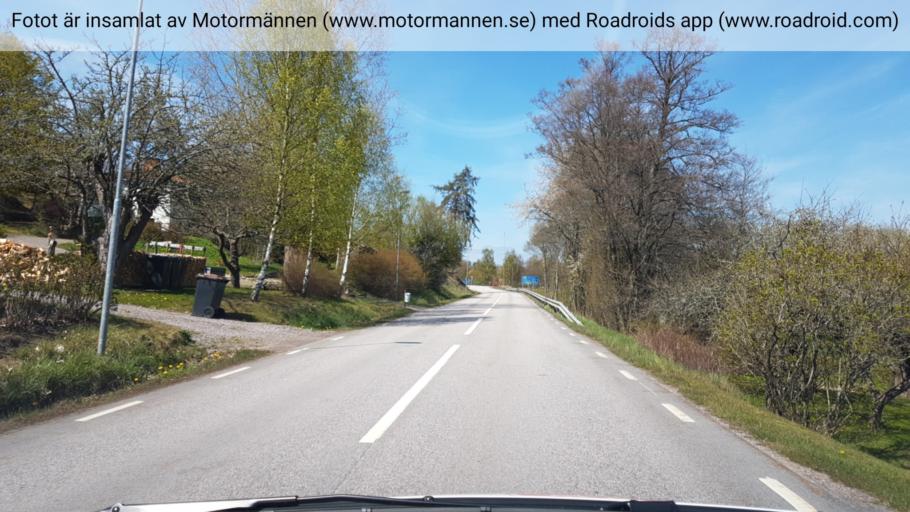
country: SE
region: Kalmar
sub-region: Vasterviks Kommun
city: Forserum
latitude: 57.9493
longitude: 16.4457
